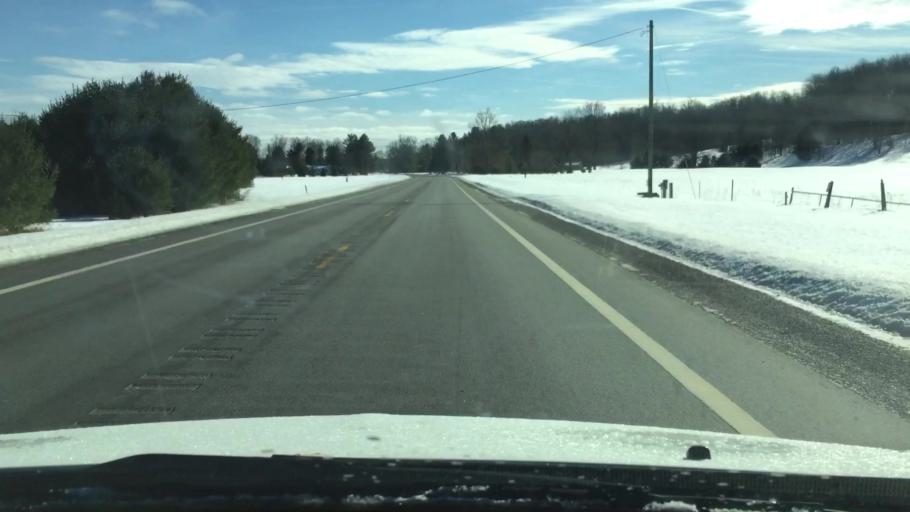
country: US
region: Michigan
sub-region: Charlevoix County
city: East Jordan
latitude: 45.0705
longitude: -85.0854
